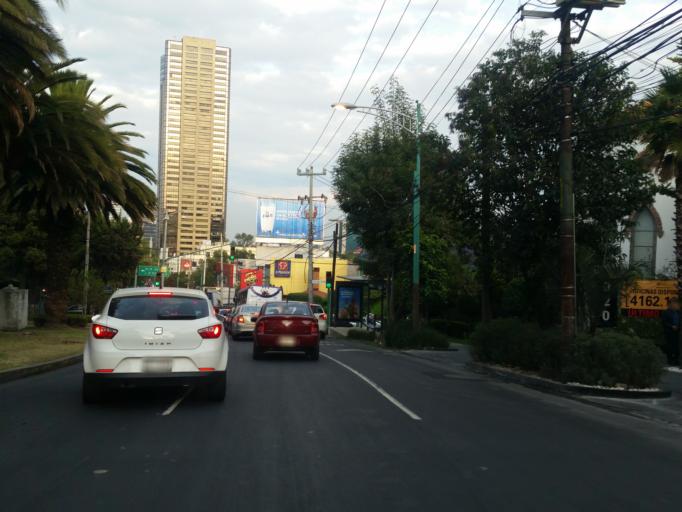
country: MX
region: Mexico City
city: Miguel Hidalgo
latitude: 19.4271
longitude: -99.2199
